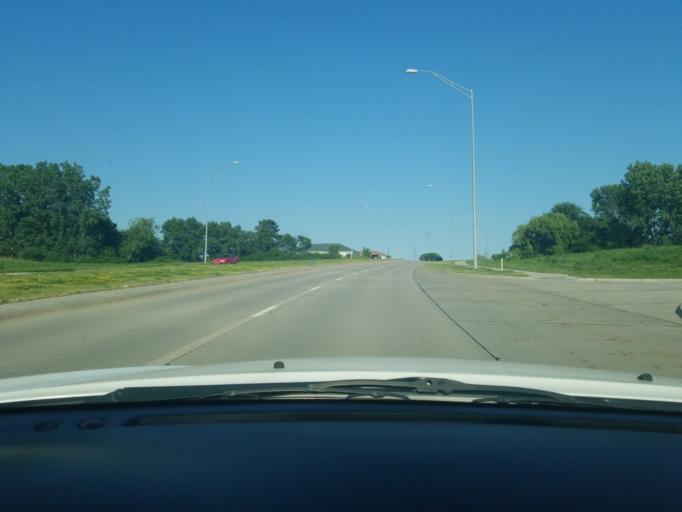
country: US
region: Nebraska
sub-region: Lancaster County
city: Lincoln
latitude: 40.7414
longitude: -96.6035
